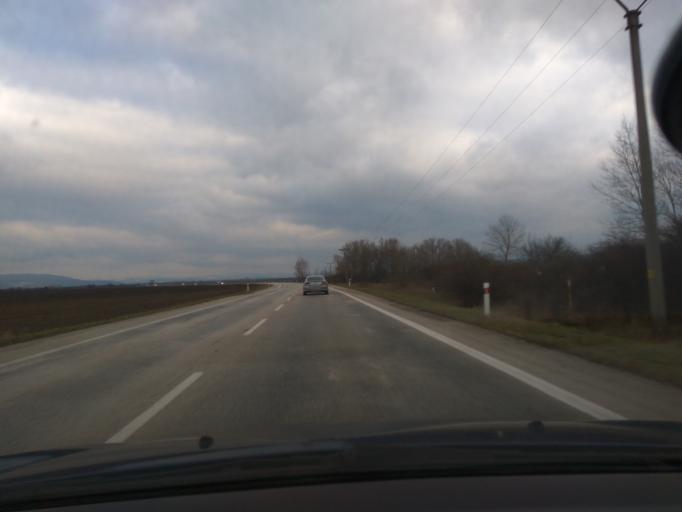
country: SK
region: Trnavsky
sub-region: Okres Trnava
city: Piestany
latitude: 48.6295
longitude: 17.8391
